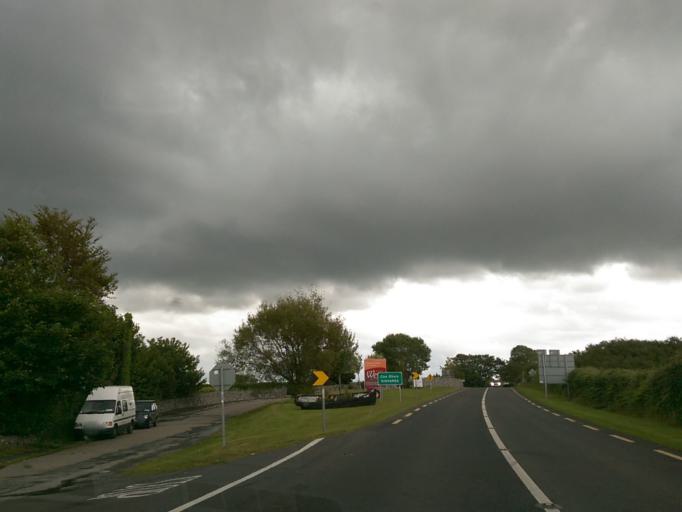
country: IE
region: Connaught
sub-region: County Galway
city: Oranmore
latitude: 53.1393
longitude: -8.9523
